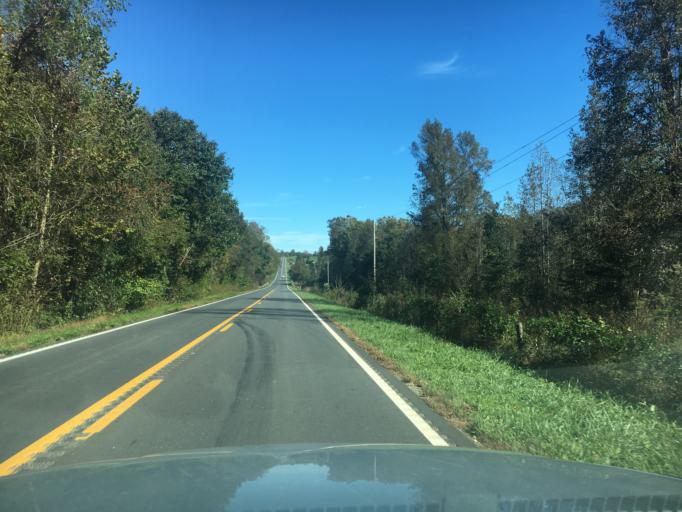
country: US
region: North Carolina
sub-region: Burke County
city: Glen Alpine
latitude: 35.6266
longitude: -81.8019
